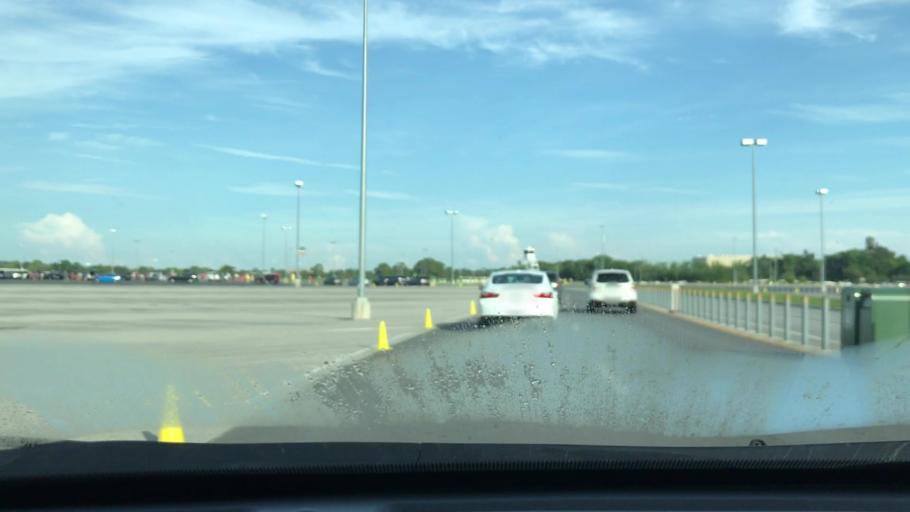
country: US
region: Florida
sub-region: Polk County
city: Citrus Ridge
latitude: 28.3509
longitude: -81.5863
